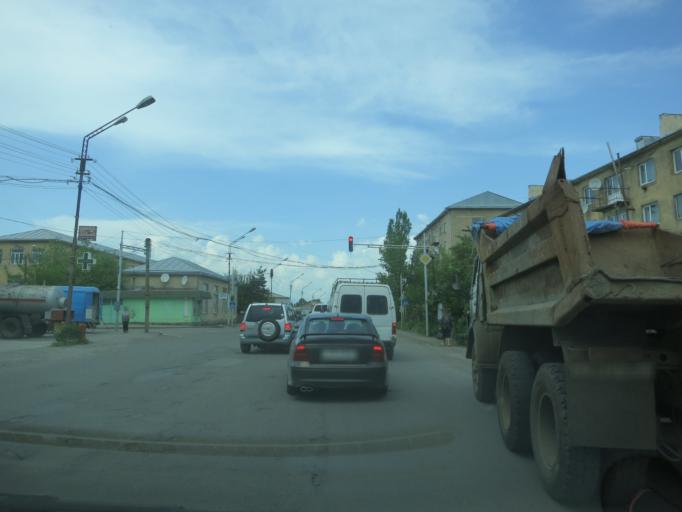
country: GE
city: Akhalk'alak'i
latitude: 41.4004
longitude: 43.4885
